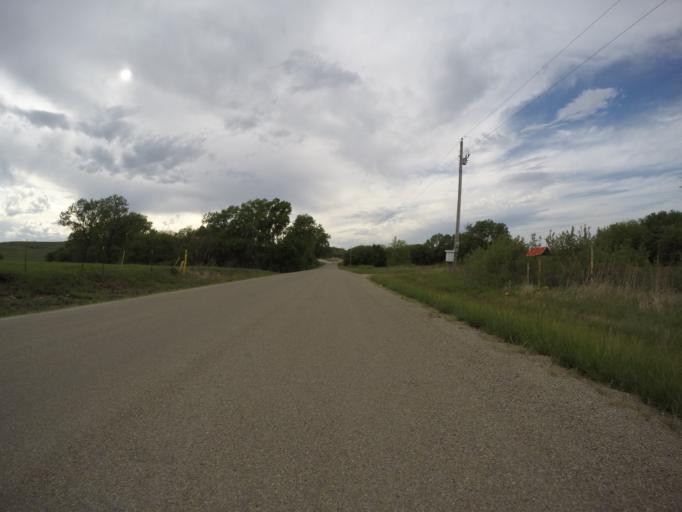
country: US
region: Kansas
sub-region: Riley County
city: Ogden
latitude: 39.0421
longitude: -96.6332
